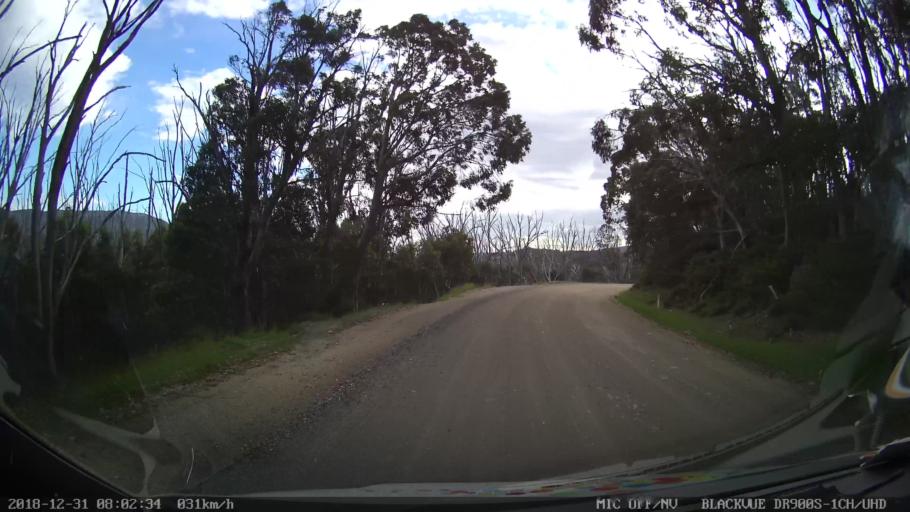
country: AU
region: New South Wales
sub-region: Snowy River
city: Jindabyne
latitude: -36.3609
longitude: 148.4018
